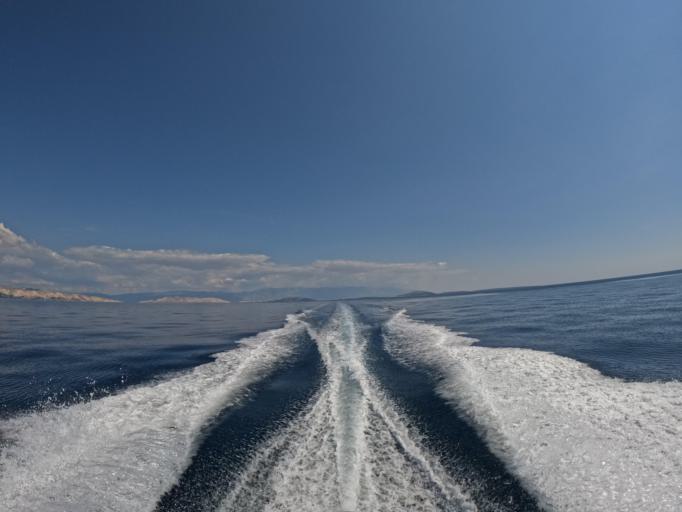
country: HR
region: Primorsko-Goranska
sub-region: Grad Krk
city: Krk
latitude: 44.9148
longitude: 14.5791
